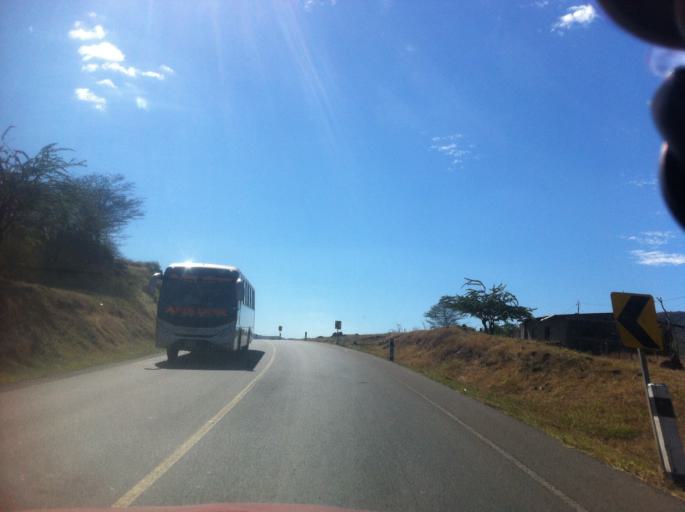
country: NI
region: Boaco
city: Teustepe
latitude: 12.3885
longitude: -85.8695
